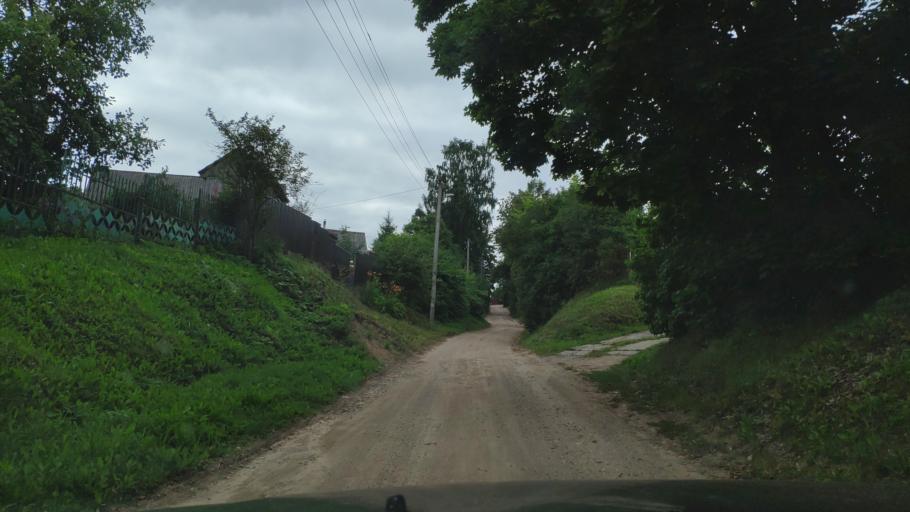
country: BY
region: Minsk
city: Khatsyezhyna
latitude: 53.9263
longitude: 27.2590
